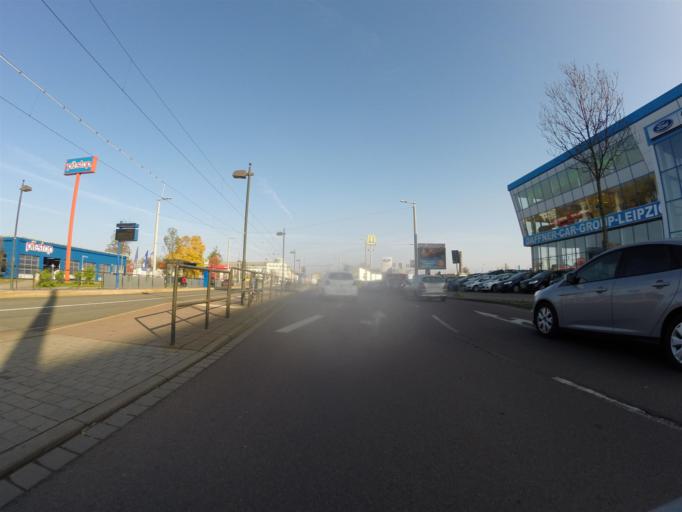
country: DE
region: Saxony
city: Leipzig
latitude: 51.3276
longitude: 12.3081
